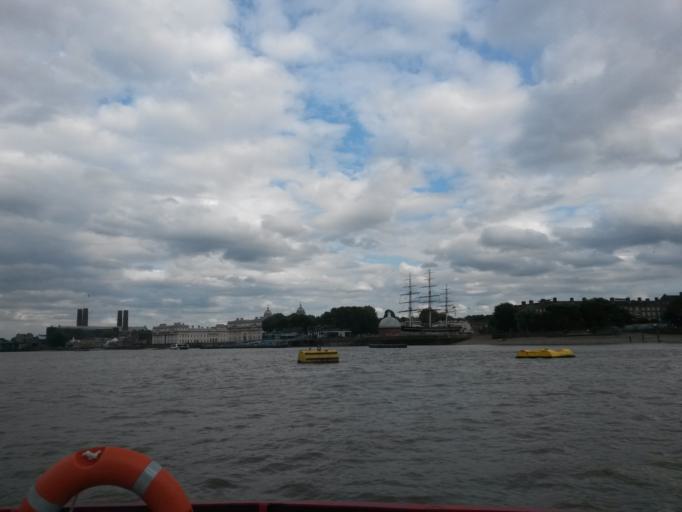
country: GB
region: England
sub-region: Greater London
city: Poplar
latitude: 51.4846
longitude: -0.0146
